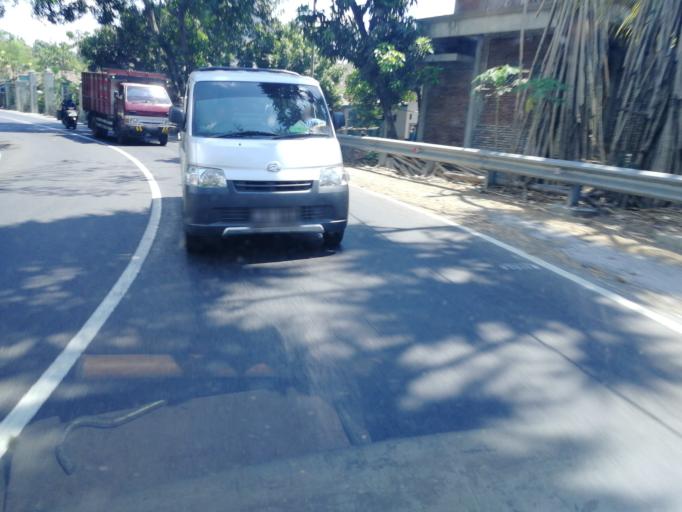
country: ID
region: West Nusa Tenggara
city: Jelateng Timur
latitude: -8.6988
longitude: 116.1058
